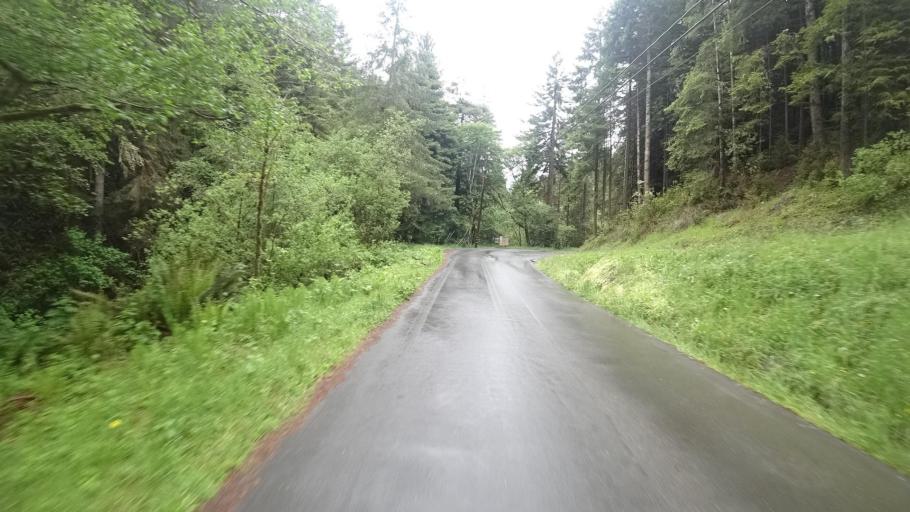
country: US
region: California
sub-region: Humboldt County
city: Bayside
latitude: 40.8165
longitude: -124.0284
